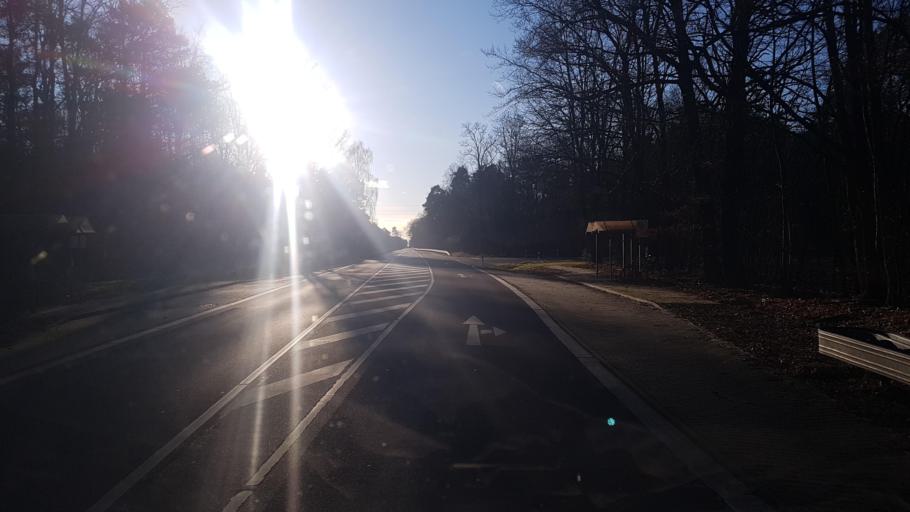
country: DE
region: Brandenburg
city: Tauer
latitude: 51.9167
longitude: 14.4917
